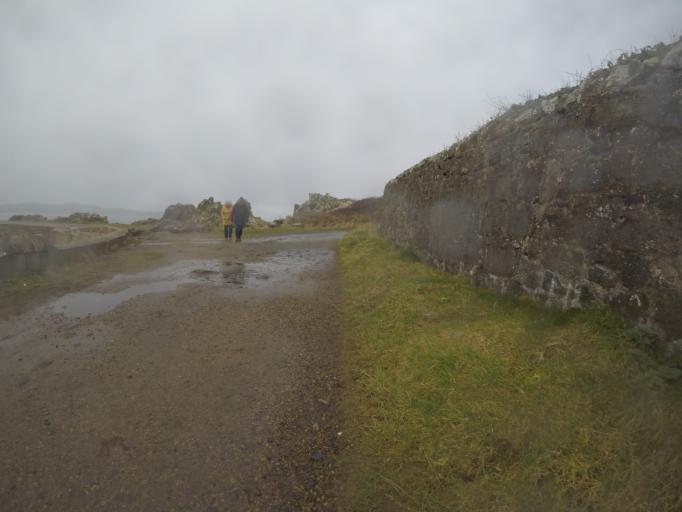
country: GB
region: Scotland
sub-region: North Ayrshire
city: Millport
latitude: 55.7018
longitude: -4.9045
